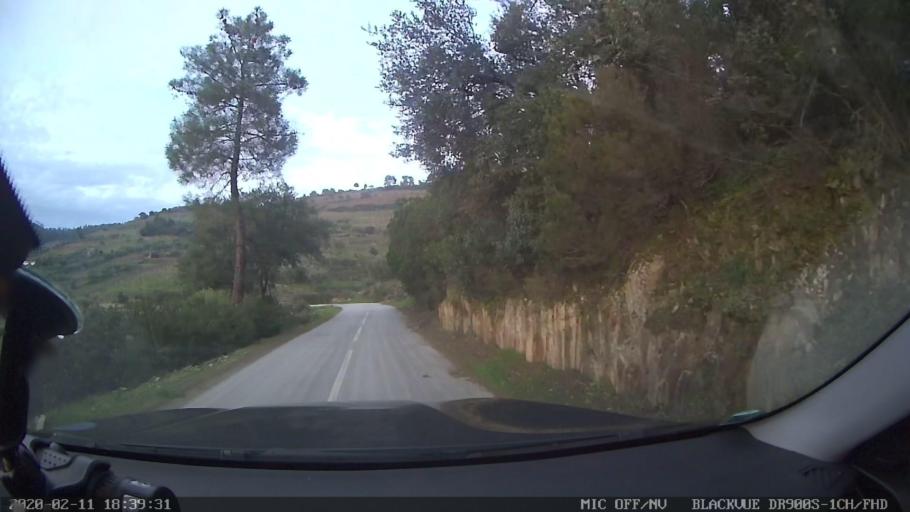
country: PT
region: Vila Real
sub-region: Sabrosa
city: Vilela
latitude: 41.1772
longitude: -7.5944
